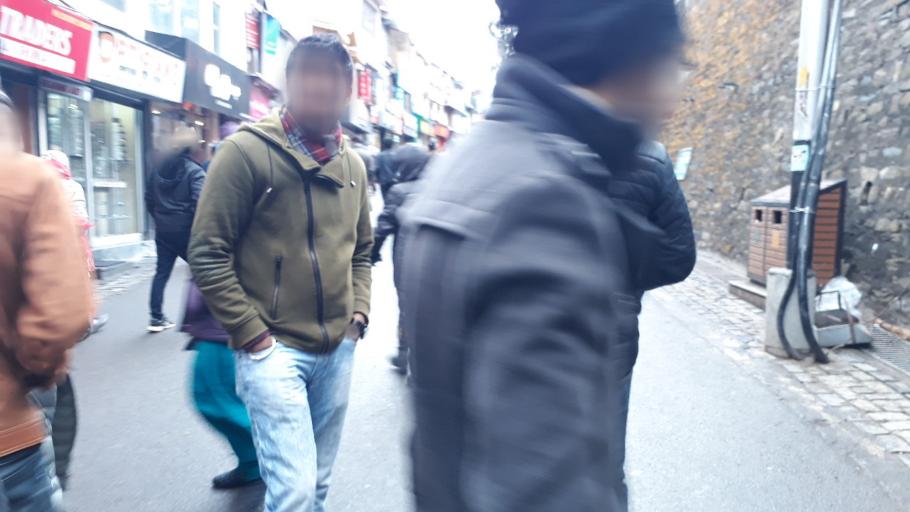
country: IN
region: Himachal Pradesh
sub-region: Shimla
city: Shimla
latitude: 31.1045
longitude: 77.1748
